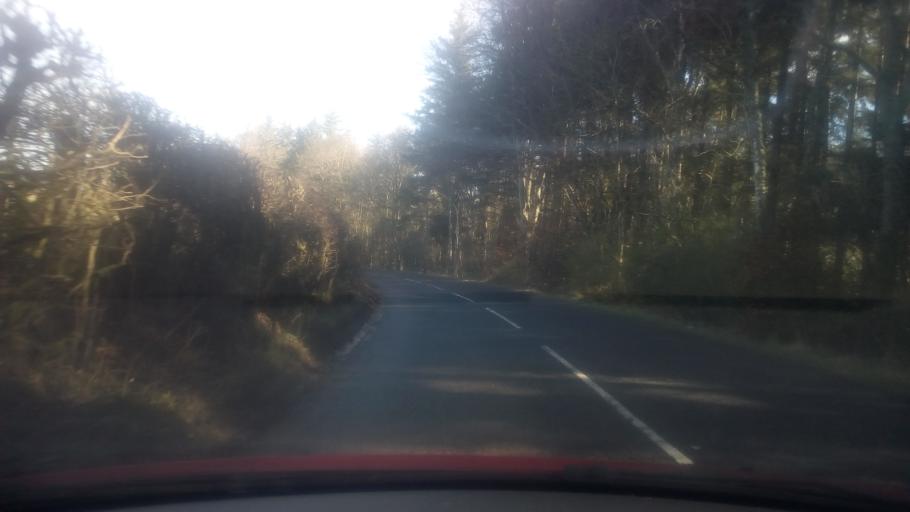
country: GB
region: Scotland
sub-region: The Scottish Borders
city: Selkirk
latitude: 55.5770
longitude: -2.8394
